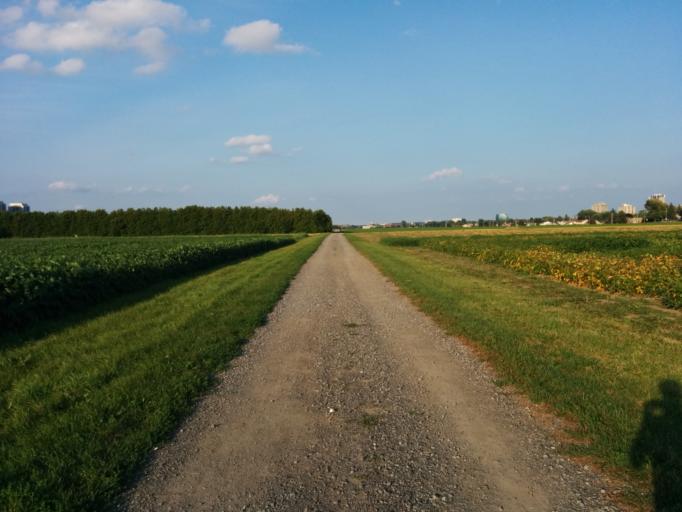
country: CA
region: Ontario
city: Ottawa
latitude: 45.3686
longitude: -75.7287
